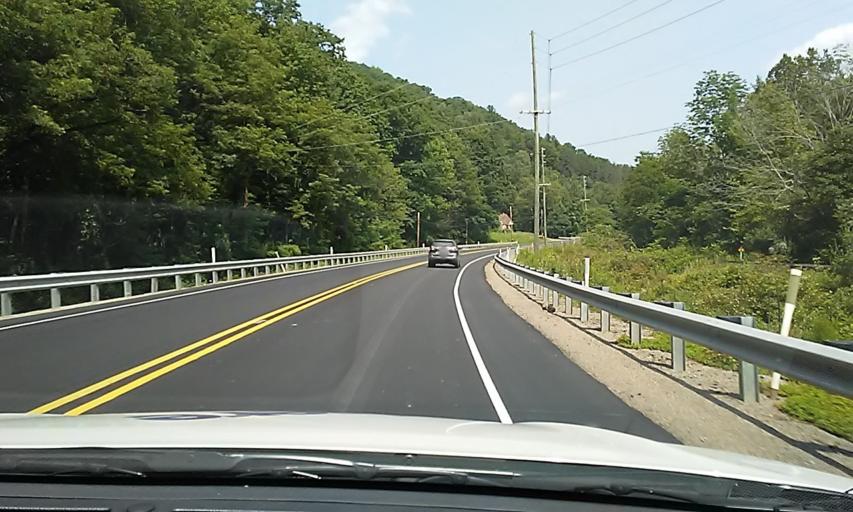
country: US
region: Pennsylvania
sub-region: Cameron County
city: Emporium
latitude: 41.4817
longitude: -78.3200
